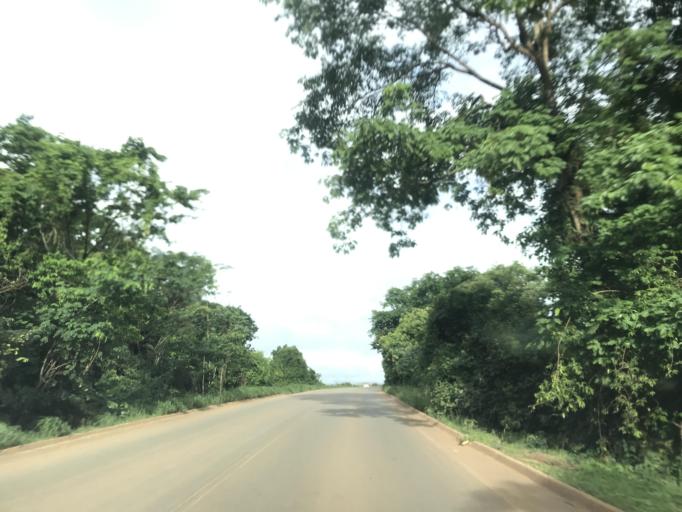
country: BR
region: Goias
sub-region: Vianopolis
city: Vianopolis
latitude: -16.5766
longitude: -48.3275
